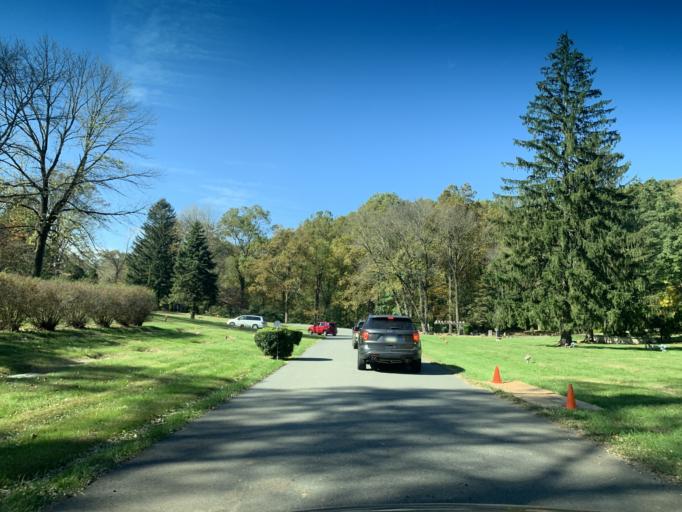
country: US
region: Pennsylvania
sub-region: Berks County
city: Mount Penn
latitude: 40.3129
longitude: -75.8914
